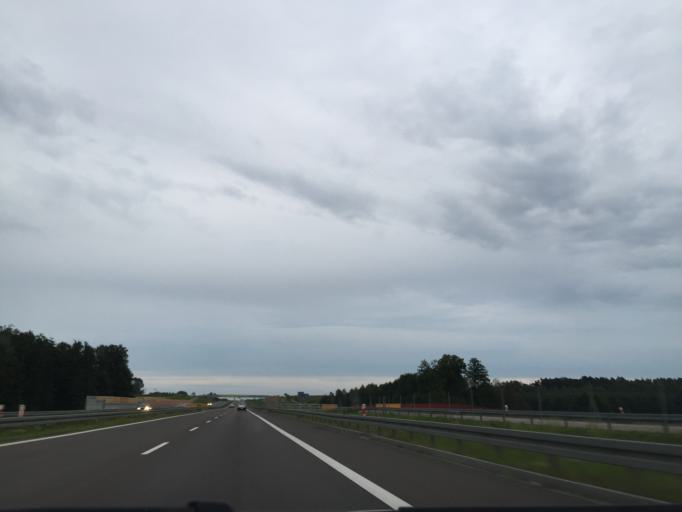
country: PL
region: Podlasie
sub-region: Powiat bialostocki
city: Tykocin
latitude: 53.1499
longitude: 22.8342
